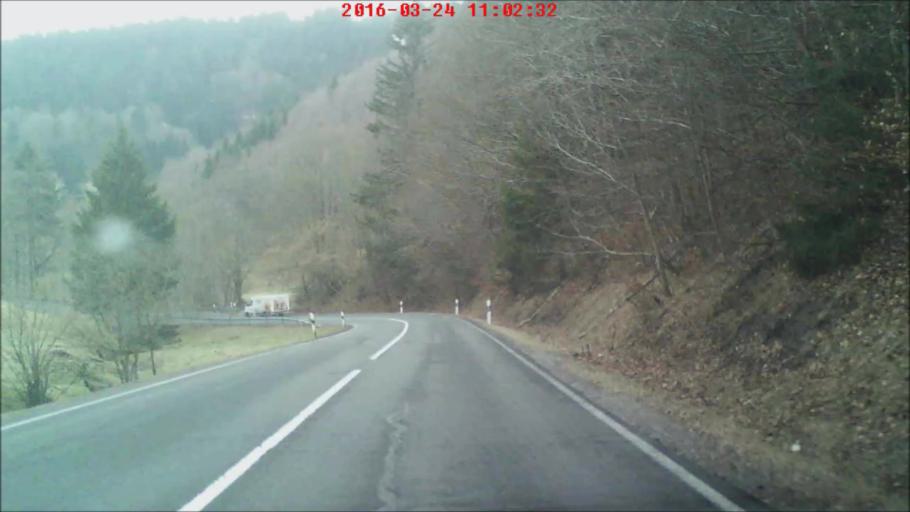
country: DE
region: Thuringia
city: Neustadt am Rennsteig
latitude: 50.5499
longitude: 10.9253
